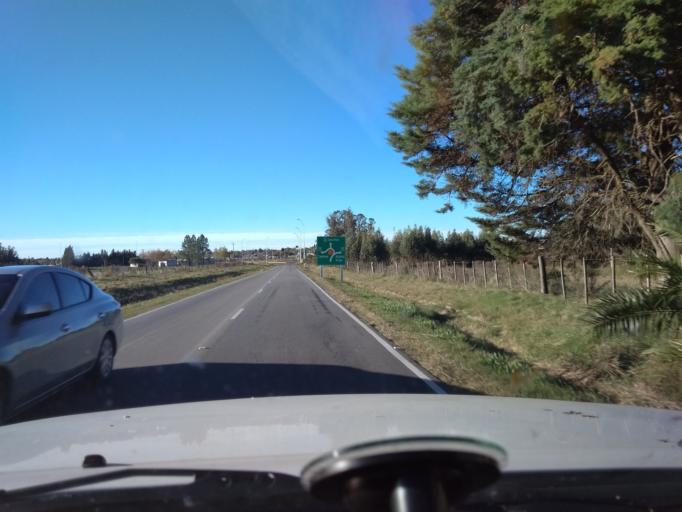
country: UY
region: Canelones
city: Santa Rosa
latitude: -34.5073
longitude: -56.0511
